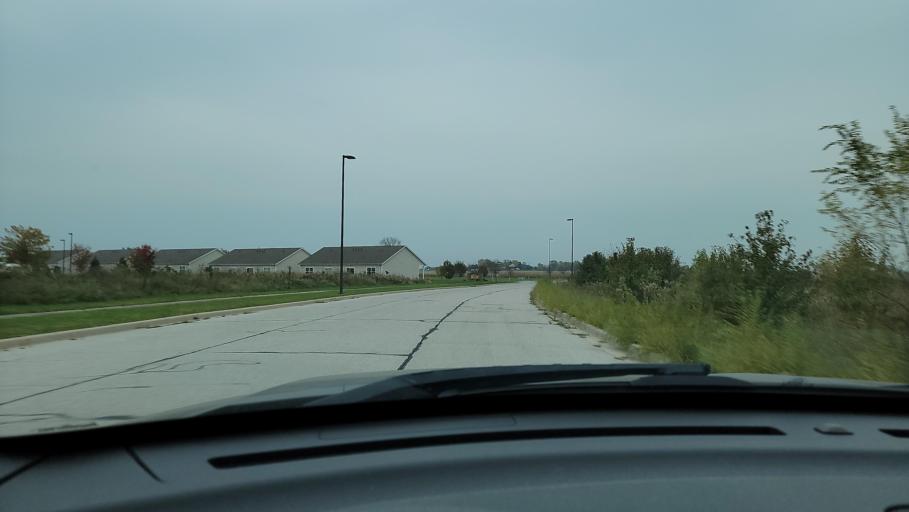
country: US
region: Indiana
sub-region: Porter County
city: Portage
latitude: 41.5447
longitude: -87.1746
